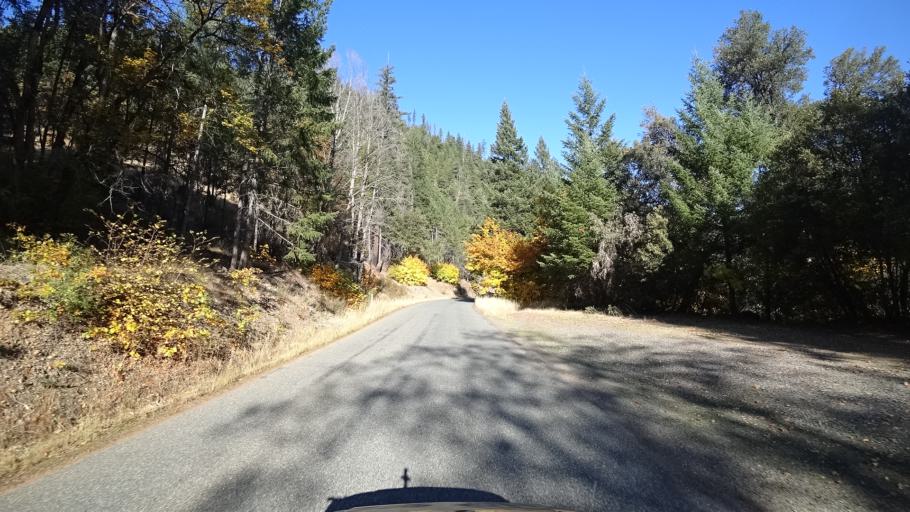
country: US
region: California
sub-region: Siskiyou County
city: Happy Camp
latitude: 41.6513
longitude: -123.1143
